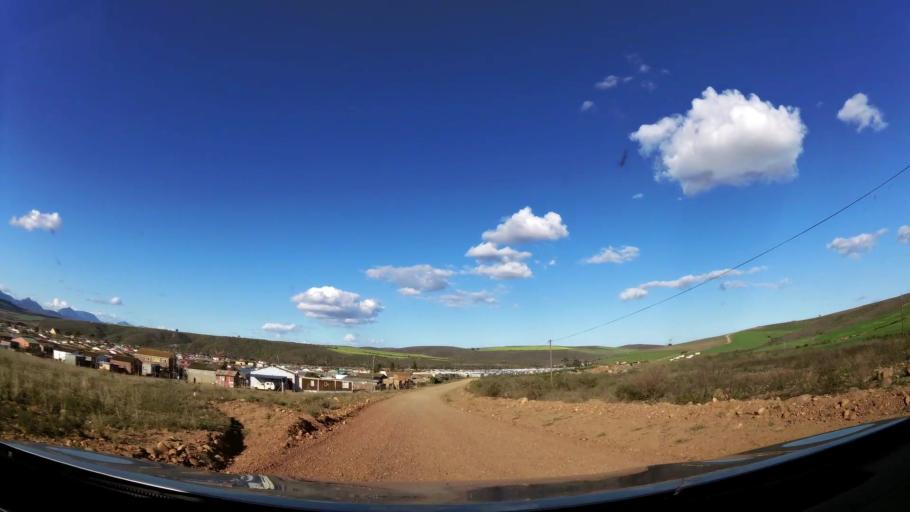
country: ZA
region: Western Cape
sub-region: Eden District Municipality
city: Riversdale
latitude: -34.1082
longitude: 20.9589
